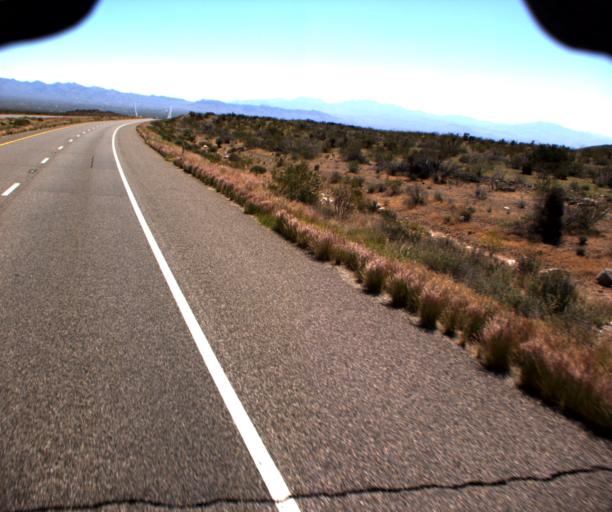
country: US
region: Arizona
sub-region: Mohave County
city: Golden Valley
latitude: 35.2291
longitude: -114.3692
